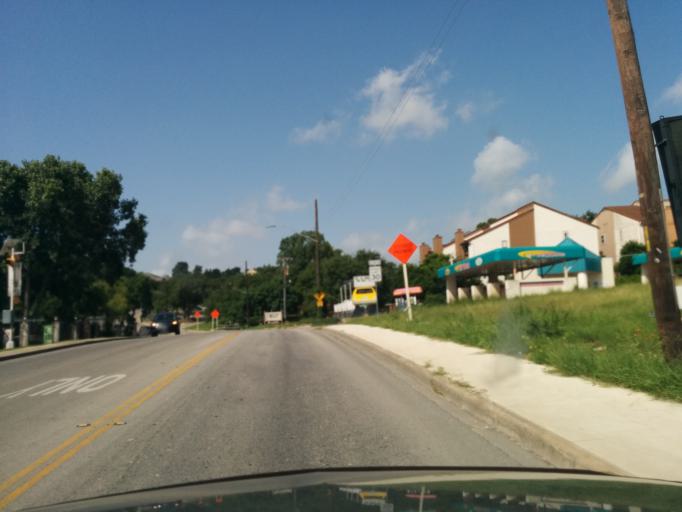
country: US
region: Texas
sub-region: Bexar County
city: Balcones Heights
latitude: 29.5176
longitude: -98.5630
